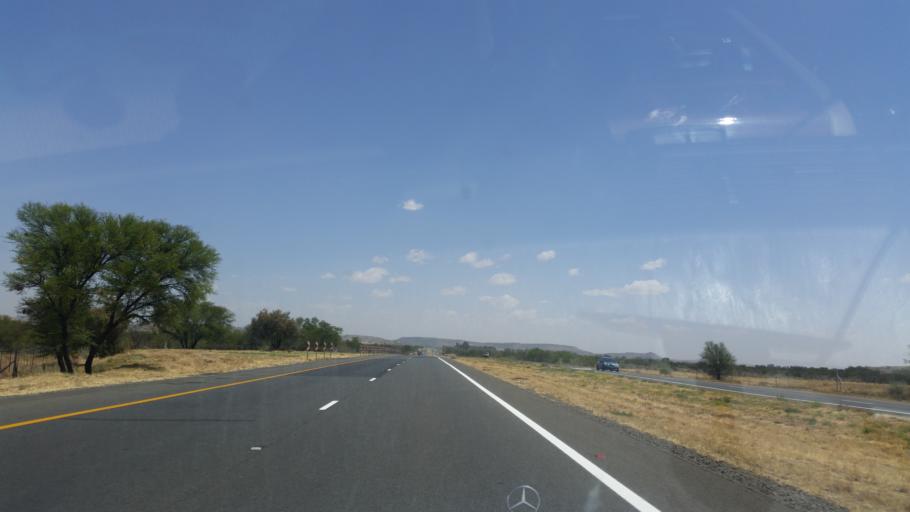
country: ZA
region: Orange Free State
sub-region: Mangaung Metropolitan Municipality
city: Bloemfontein
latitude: -28.9585
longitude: 26.3720
